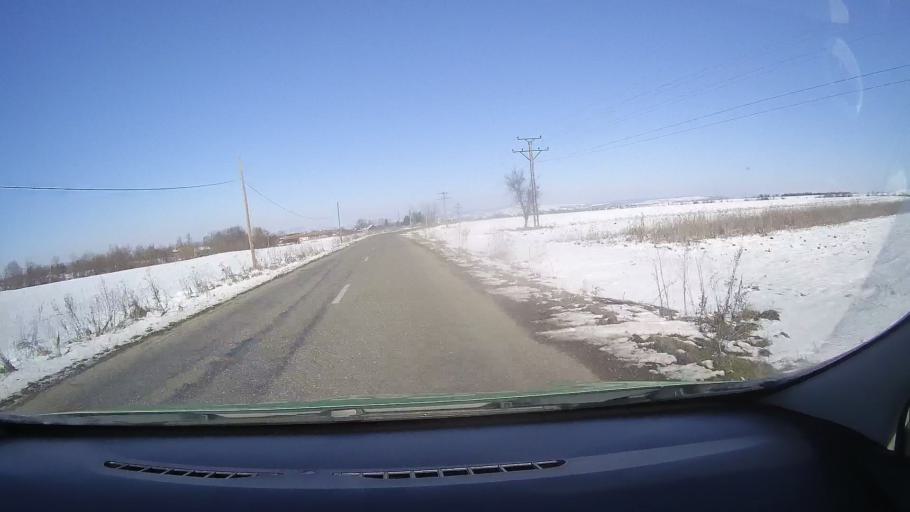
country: RO
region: Brasov
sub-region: Comuna Harseni
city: Harseni
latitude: 45.7773
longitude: 25.0010
